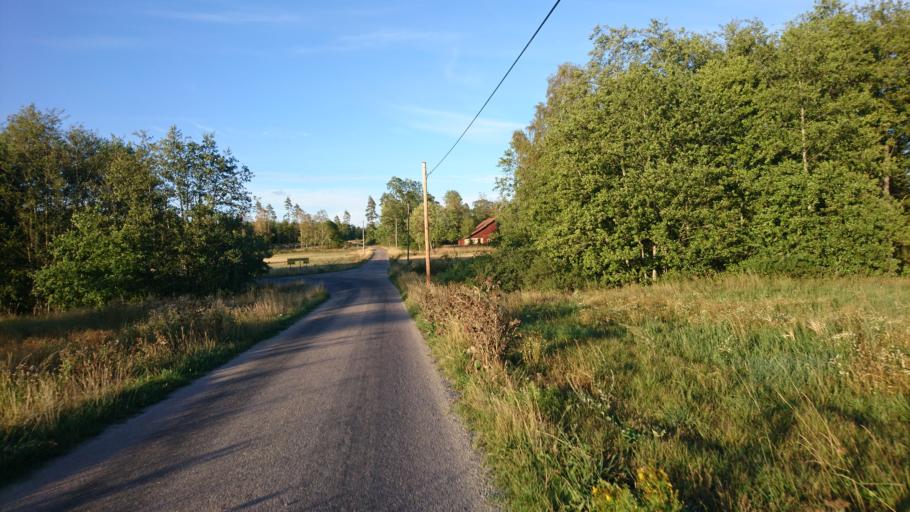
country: SE
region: Soedermanland
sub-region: Strangnas Kommun
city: Stallarholmen
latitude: 59.4000
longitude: 17.3074
